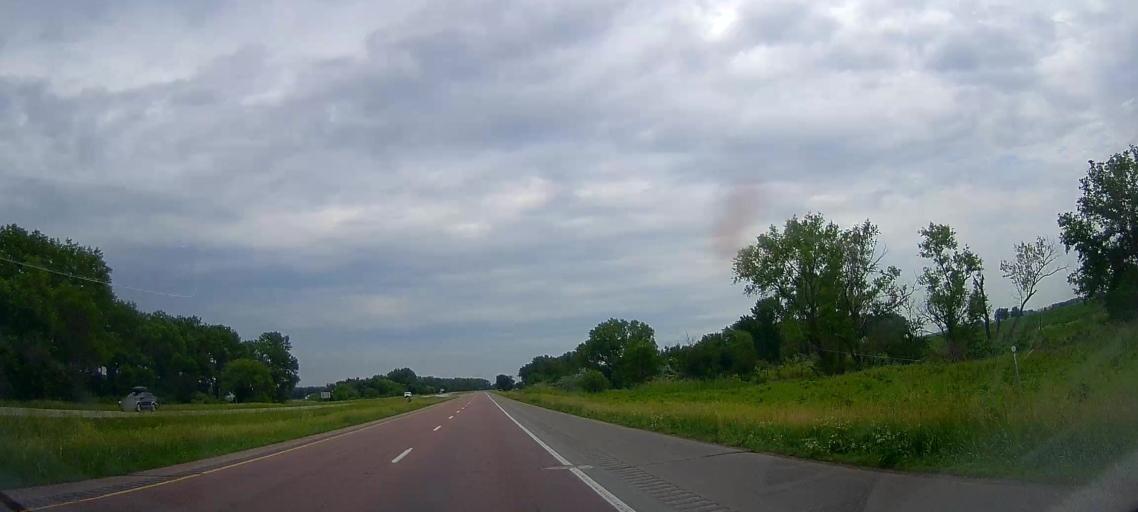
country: US
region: Iowa
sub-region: Woodbury County
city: Sergeant Bluff
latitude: 42.2805
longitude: -96.2763
